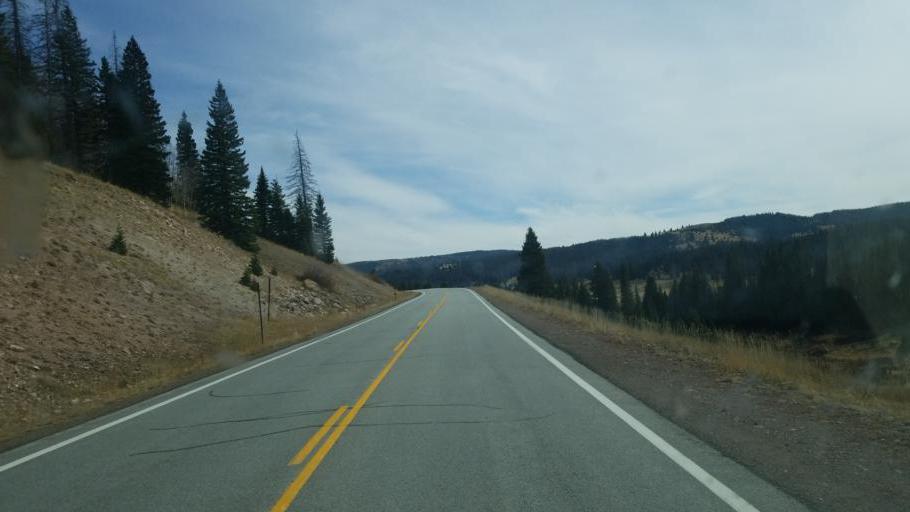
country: US
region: New Mexico
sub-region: Rio Arriba County
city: Chama
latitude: 37.0209
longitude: -106.4421
